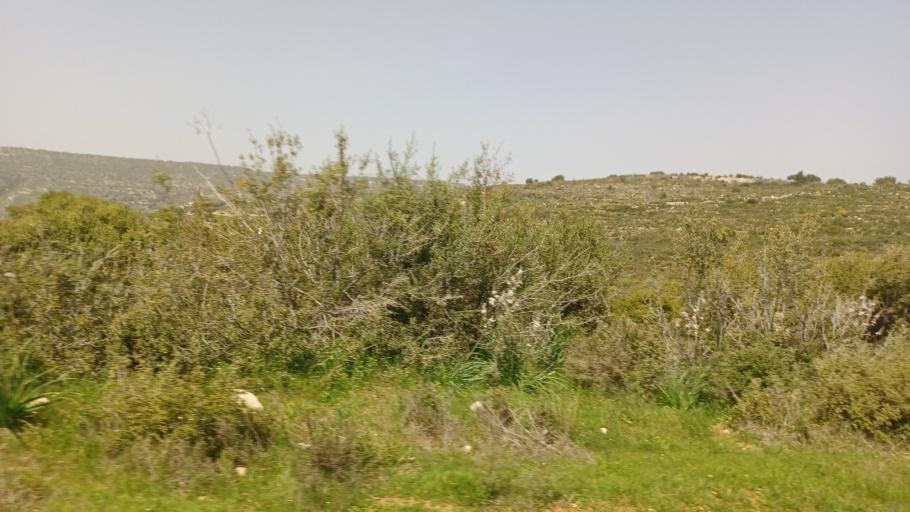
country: CY
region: Limassol
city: Pachna
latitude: 34.7540
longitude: 32.7490
